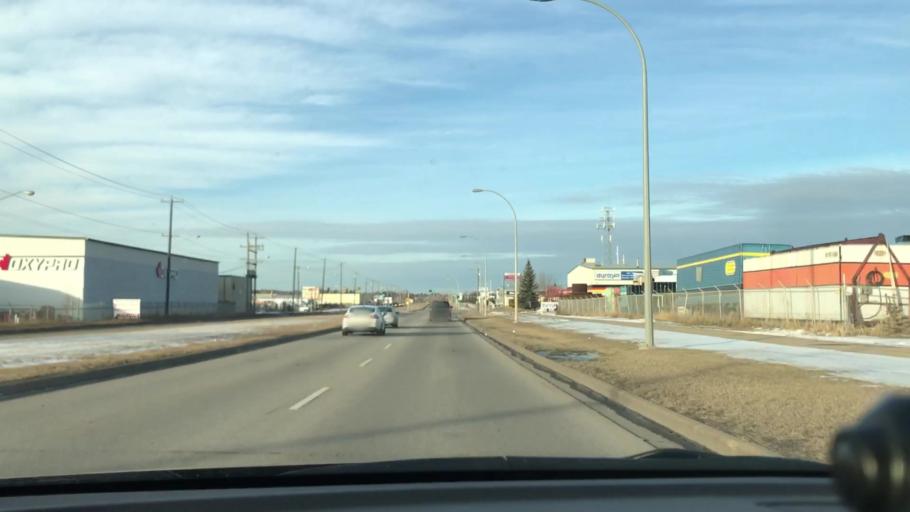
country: CA
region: Alberta
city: Edmonton
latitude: 53.4919
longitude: -113.4670
